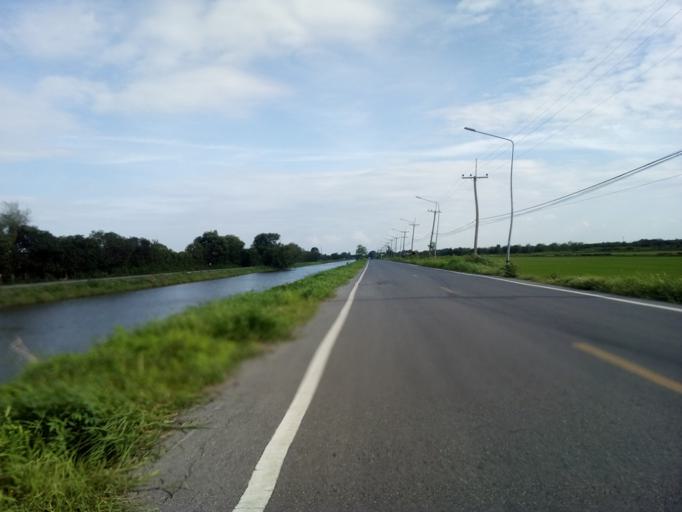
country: TH
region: Pathum Thani
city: Nong Suea
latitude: 14.0729
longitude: 100.8463
